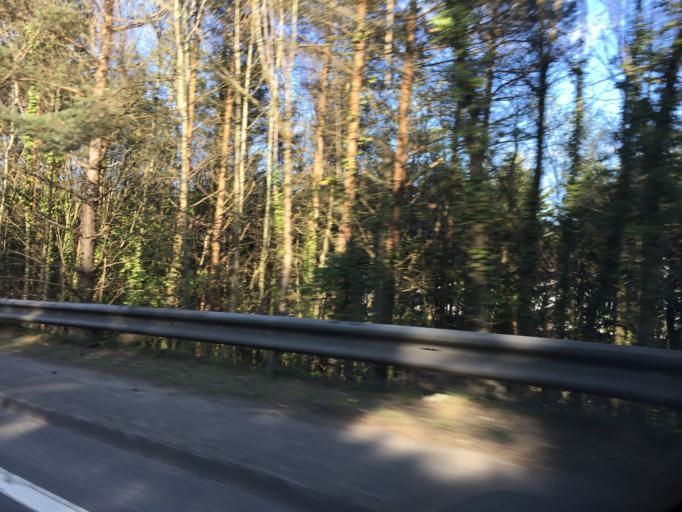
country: GB
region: Wales
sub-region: Torfaen County Borough
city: New Inn
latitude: 51.6753
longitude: -3.0161
